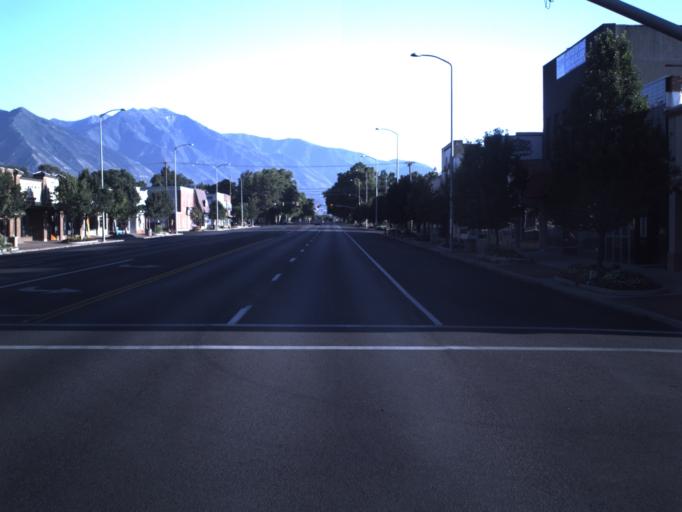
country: US
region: Utah
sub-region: Utah County
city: Spanish Fork
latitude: 40.1125
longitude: -111.6549
